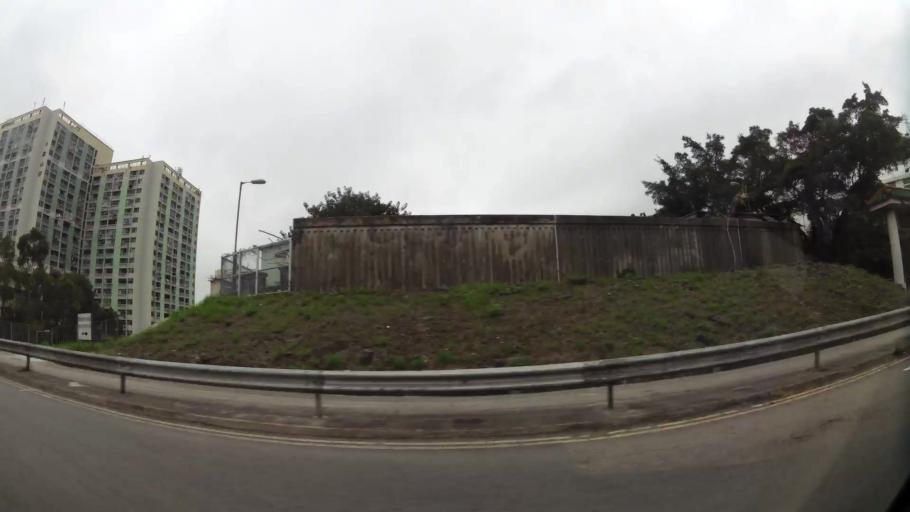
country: HK
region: Tsuen Wan
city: Tsuen Wan
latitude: 22.3801
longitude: 114.1317
